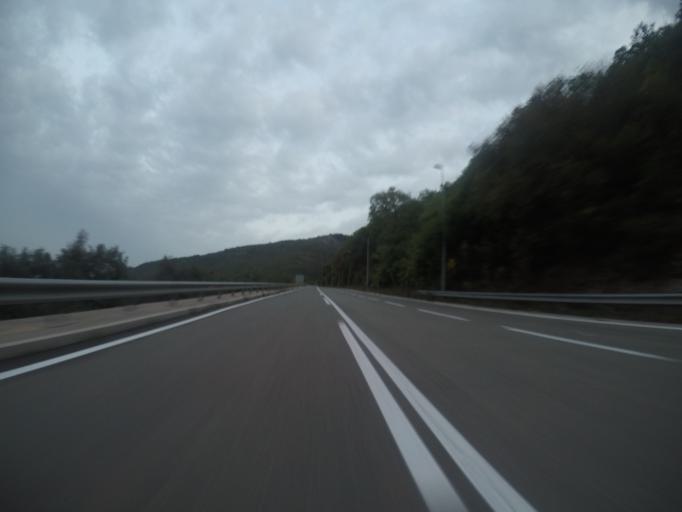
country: ME
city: Petrovac na Moru
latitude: 42.2081
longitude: 18.9486
